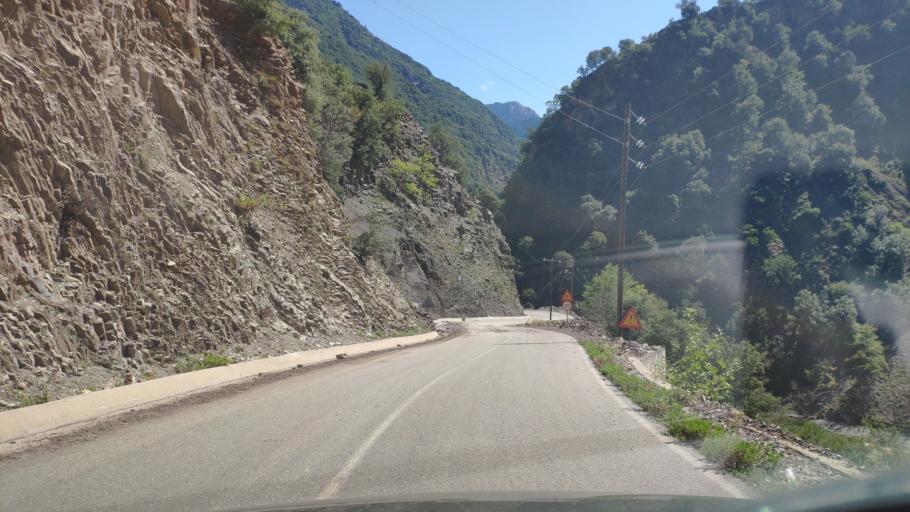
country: GR
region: Central Greece
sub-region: Nomos Evrytanias
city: Kerasochori
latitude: 39.0897
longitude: 21.5995
